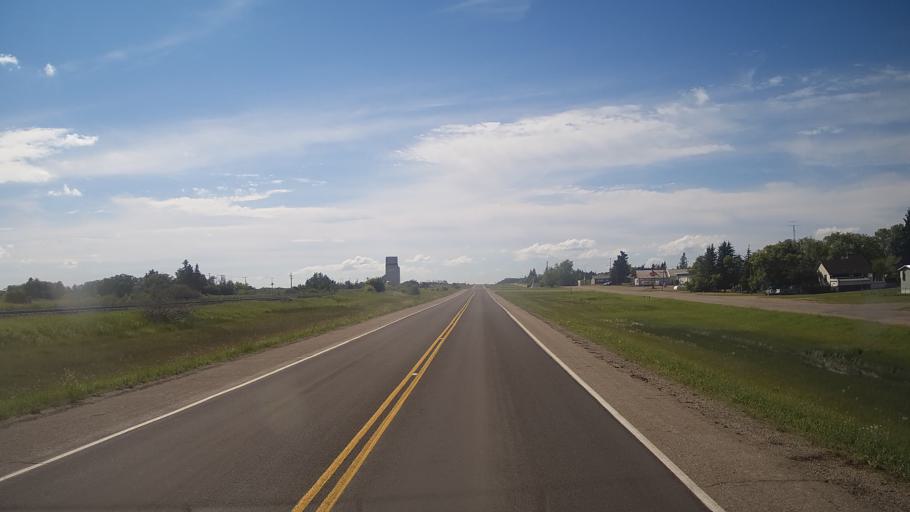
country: CA
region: Saskatchewan
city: Foam Lake
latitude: 51.2609
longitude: -103.7335
